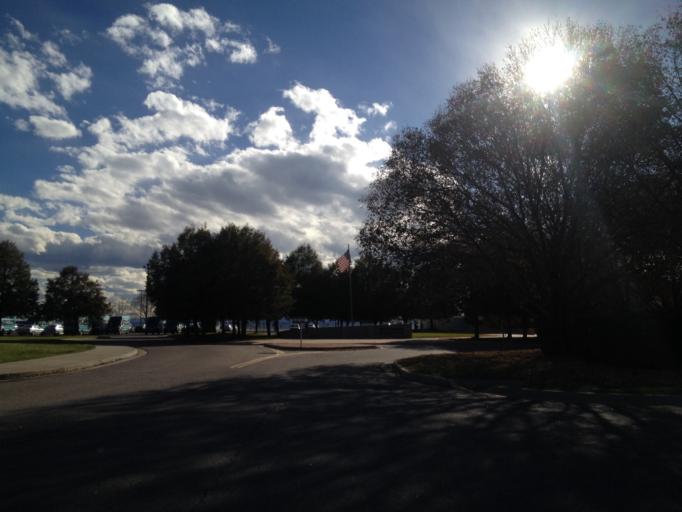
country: US
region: Colorado
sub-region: Broomfield County
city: Broomfield
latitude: 39.9103
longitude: -105.1104
